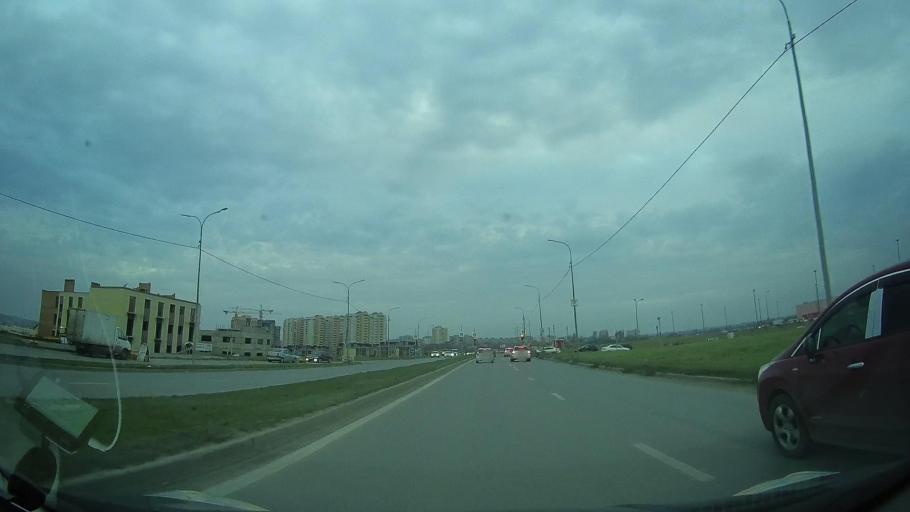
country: RU
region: Rostov
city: Temernik
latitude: 47.3085
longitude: 39.7269
